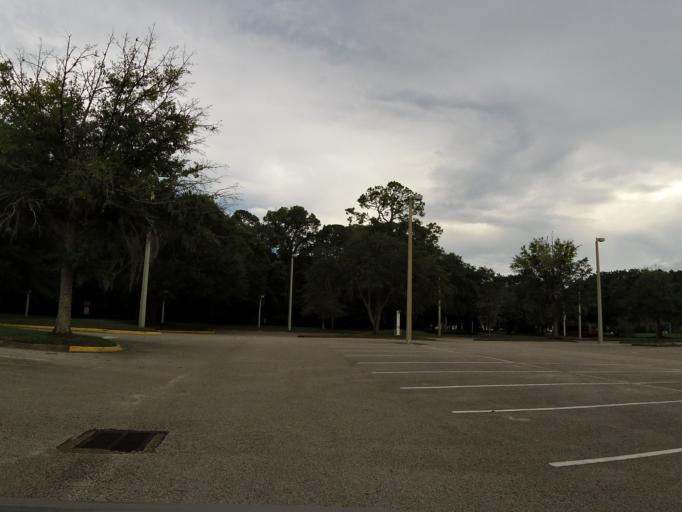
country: US
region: Florida
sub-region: Duval County
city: Jacksonville
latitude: 30.2987
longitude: -81.7184
